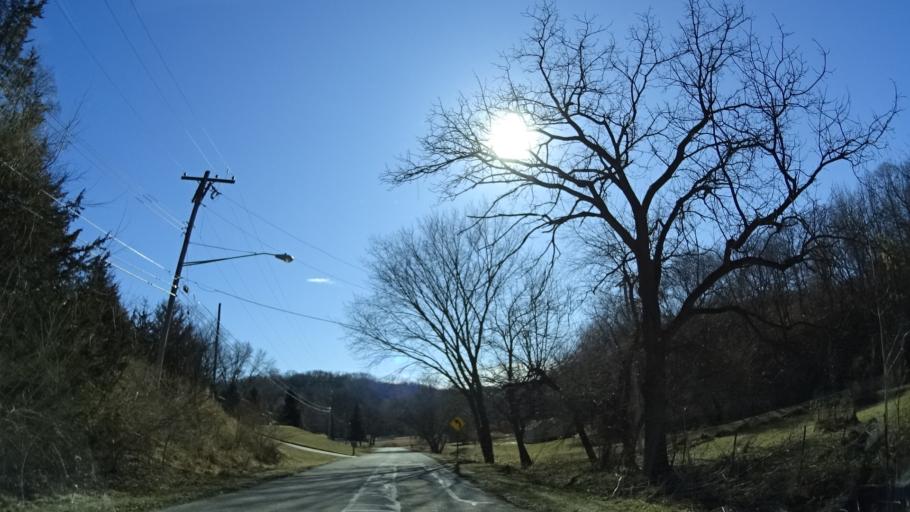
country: US
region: Nebraska
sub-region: Sarpy County
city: Bellevue
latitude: 41.1560
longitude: -95.8951
